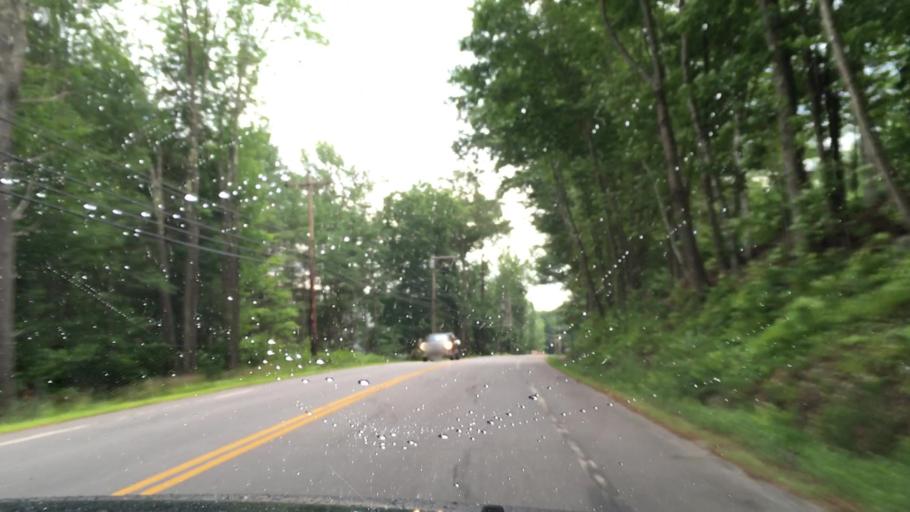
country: US
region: New Hampshire
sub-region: Belknap County
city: Meredith
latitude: 43.6767
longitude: -71.5074
